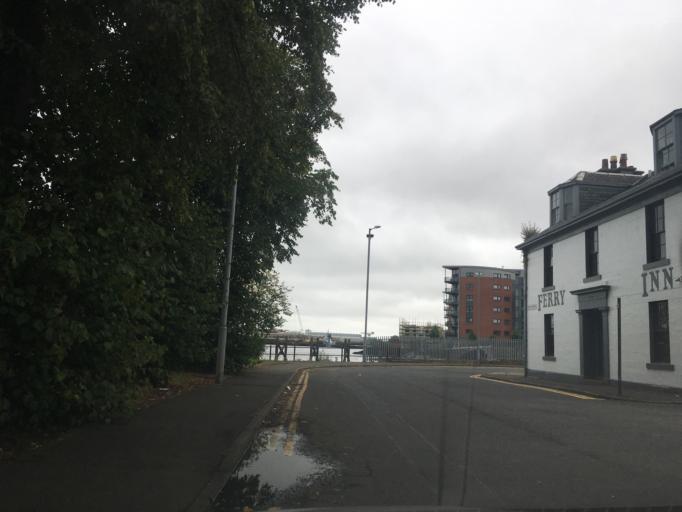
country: GB
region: Scotland
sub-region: Renfrewshire
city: Renfrew
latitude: 55.8859
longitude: -4.3836
